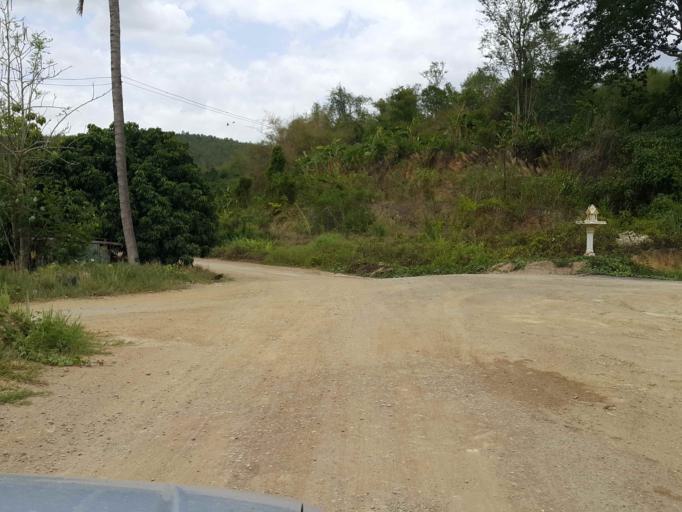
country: TH
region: Chiang Mai
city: Hang Dong
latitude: 18.7462
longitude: 98.8866
